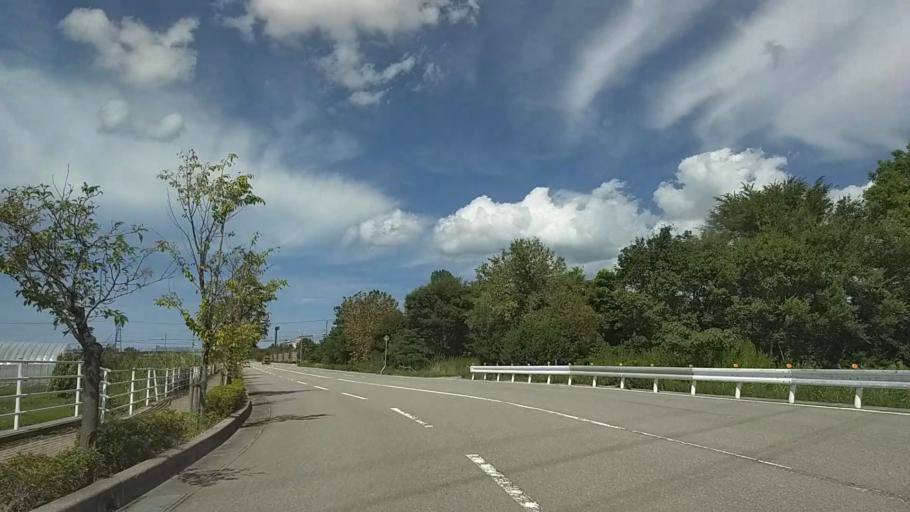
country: JP
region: Ishikawa
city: Kanazawa-shi
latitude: 36.5935
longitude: 136.6571
